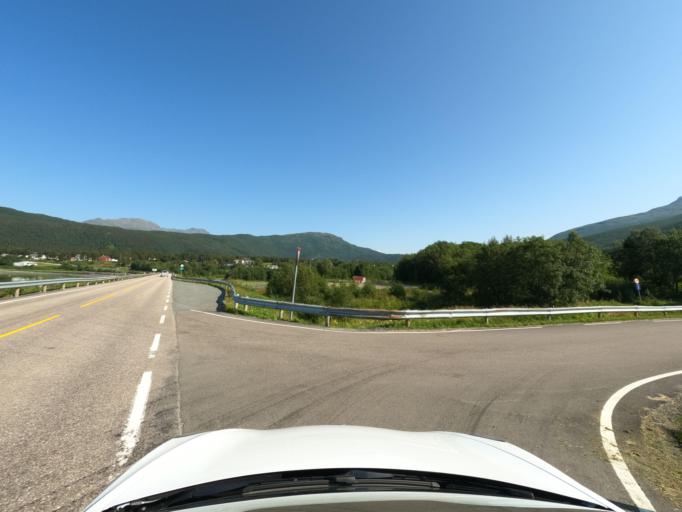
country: NO
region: Nordland
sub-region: Narvik
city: Narvik
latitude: 68.4019
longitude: 17.2943
